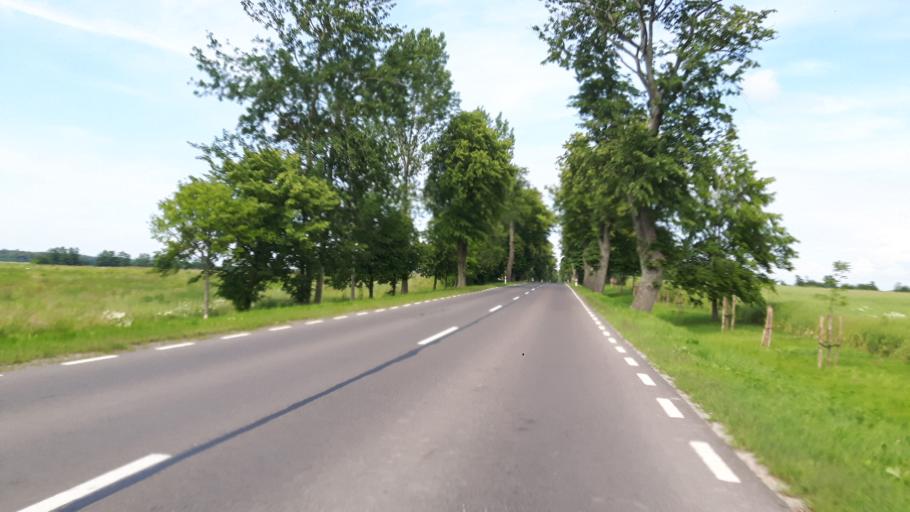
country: PL
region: Warmian-Masurian Voivodeship
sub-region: Powiat braniewski
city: Braniewo
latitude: 54.4159
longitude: 19.8730
